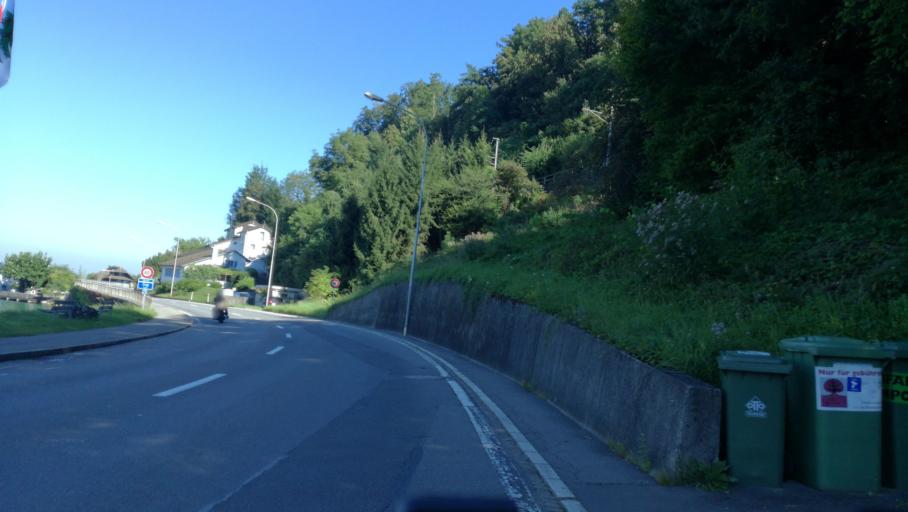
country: CH
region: Zug
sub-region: Zug
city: Walchwil
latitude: 47.1105
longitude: 8.5028
